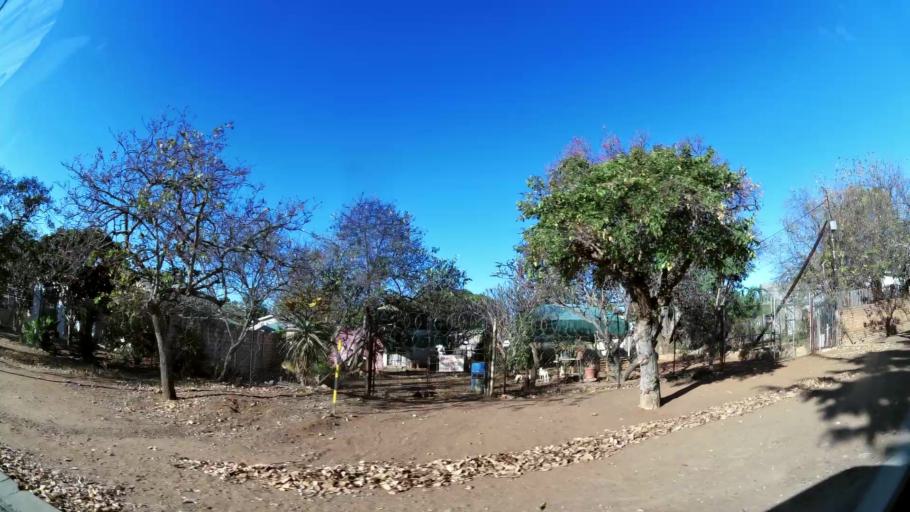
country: ZA
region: Limpopo
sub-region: Capricorn District Municipality
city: Polokwane
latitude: -23.8925
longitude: 29.4632
